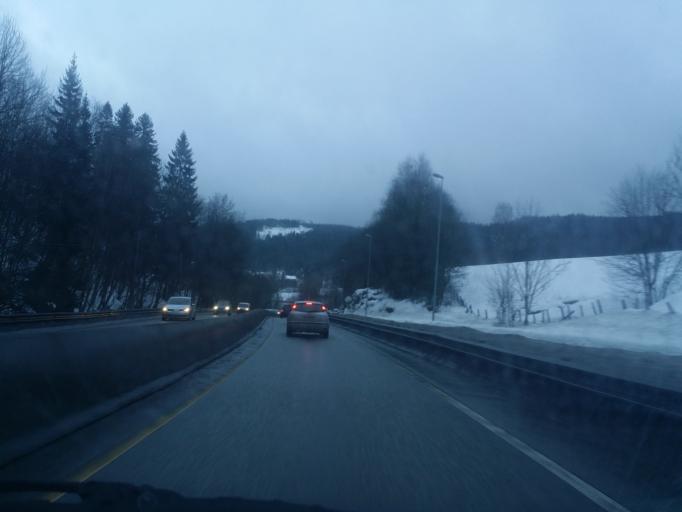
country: NO
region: Akershus
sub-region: Baerum
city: Skui
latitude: 59.9427
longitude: 10.4036
